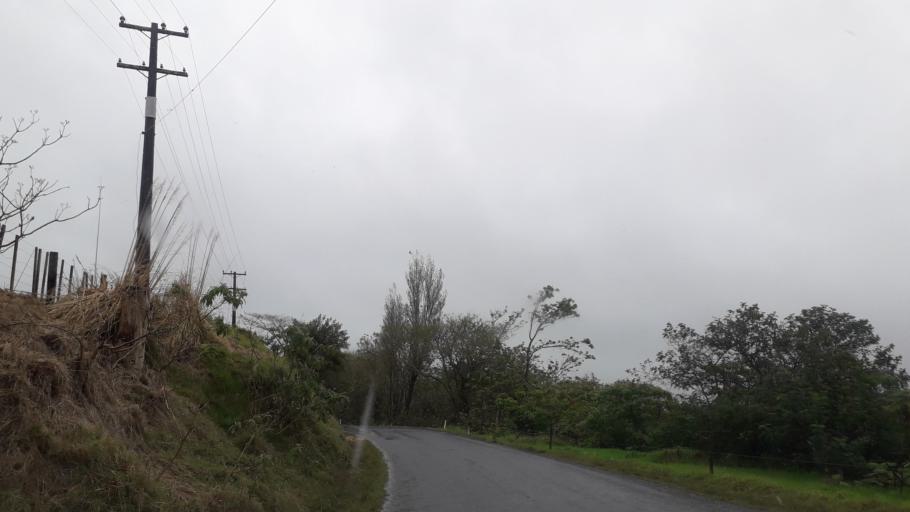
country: NZ
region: Northland
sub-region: Far North District
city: Kaitaia
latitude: -35.4052
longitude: 173.3772
